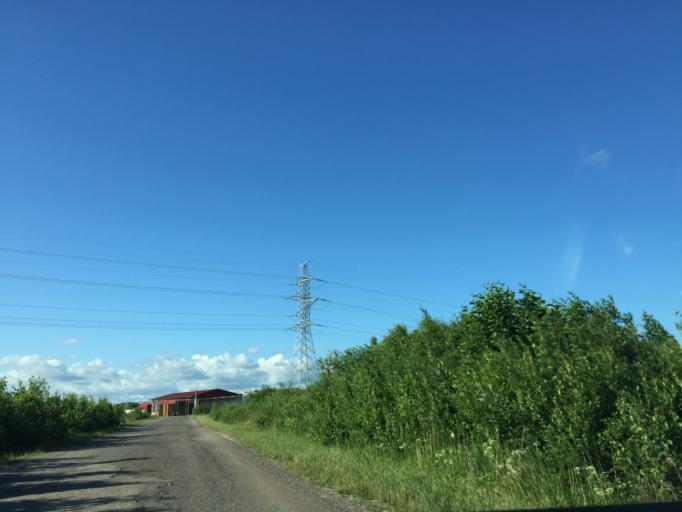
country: LV
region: Ventspils
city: Ventspils
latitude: 57.3993
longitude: 21.6492
